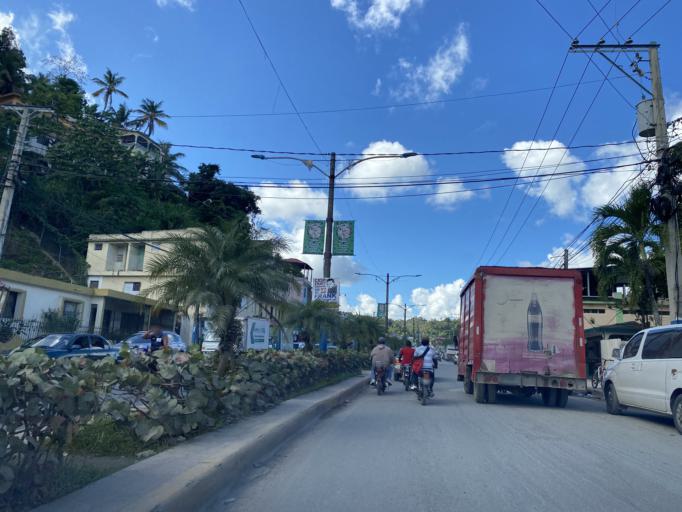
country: DO
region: Samana
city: Samana
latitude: 19.2037
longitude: -69.3408
